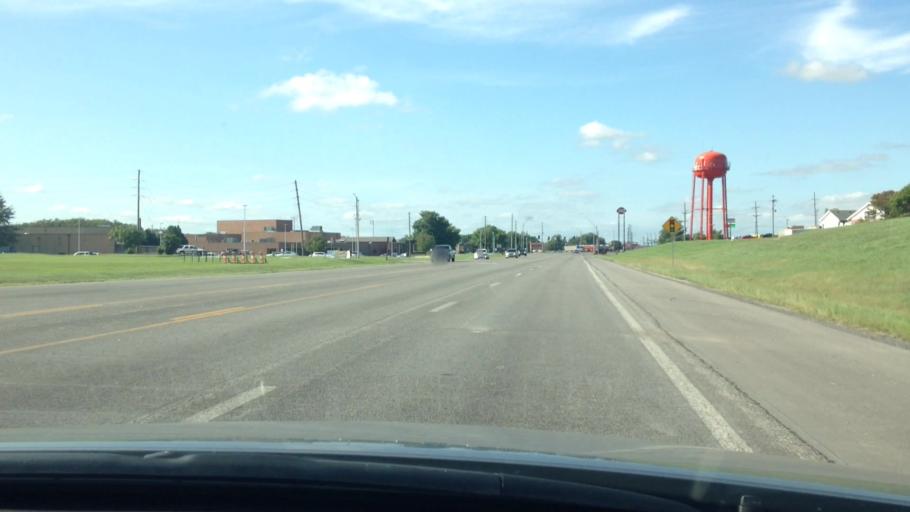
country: US
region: Missouri
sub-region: Platte County
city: Platte City
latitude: 39.3554
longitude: -94.7684
